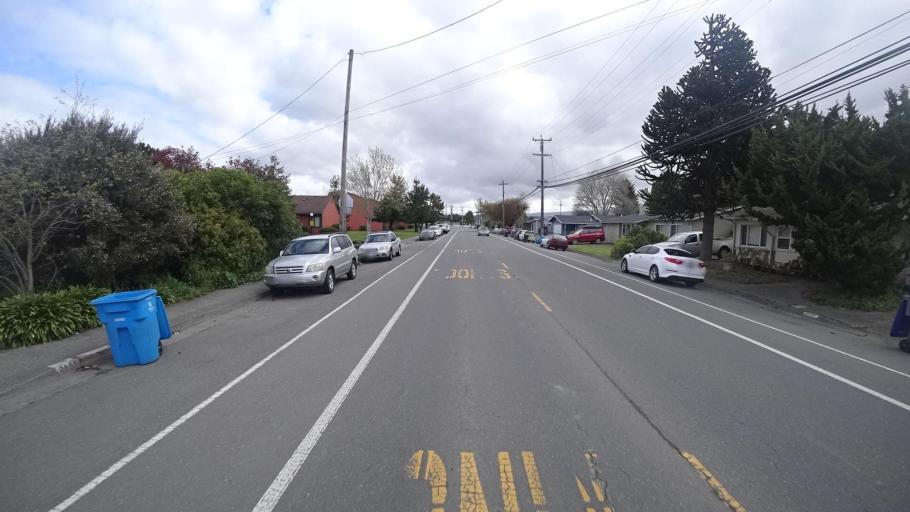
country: US
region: California
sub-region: Humboldt County
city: Arcata
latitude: 40.8854
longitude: -124.0896
